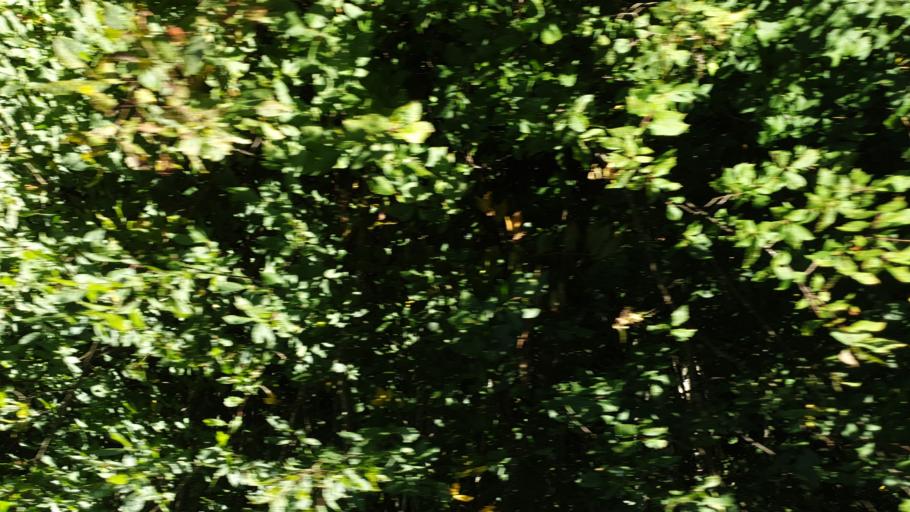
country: NO
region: Sor-Trondelag
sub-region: Meldal
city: Meldal
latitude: 63.1729
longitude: 9.7489
